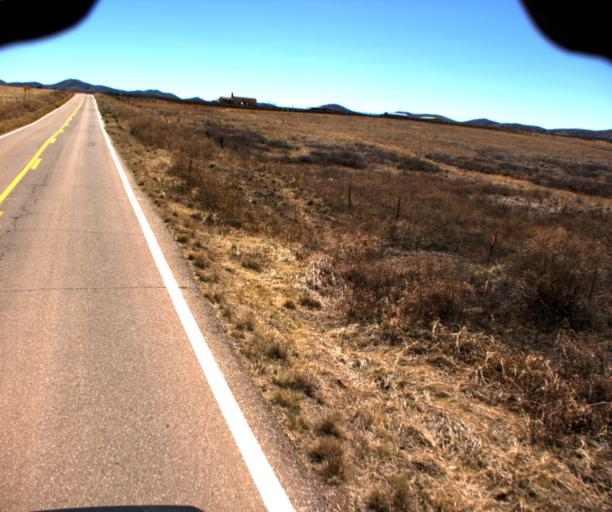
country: US
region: Arizona
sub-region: Cochise County
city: Huachuca City
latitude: 31.6137
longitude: -110.5871
